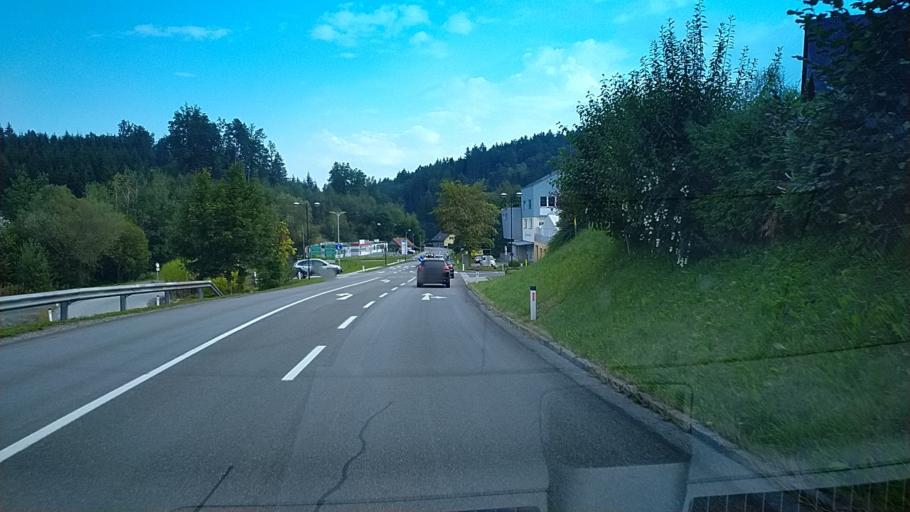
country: AT
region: Styria
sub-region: Politischer Bezirk Deutschlandsberg
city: Sankt Peter im Sulmtal
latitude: 46.7371
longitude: 15.2403
